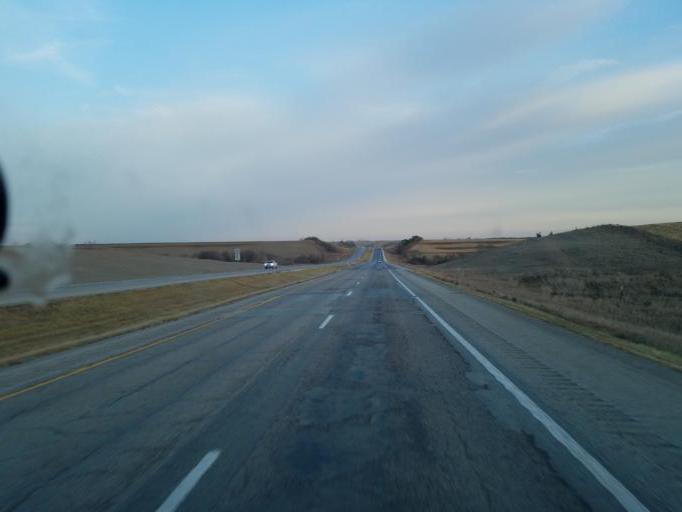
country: US
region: Iowa
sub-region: Harrison County
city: Missouri Valley
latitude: 41.4987
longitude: -95.7616
